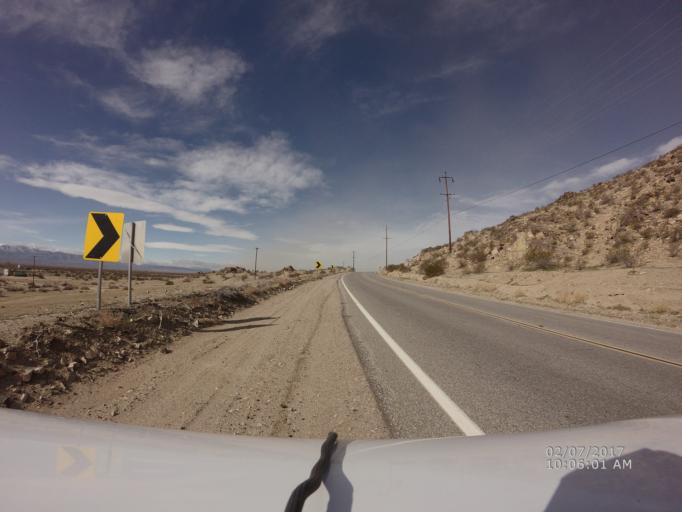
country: US
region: California
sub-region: Los Angeles County
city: Lake Los Angeles
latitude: 34.5795
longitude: -117.7317
